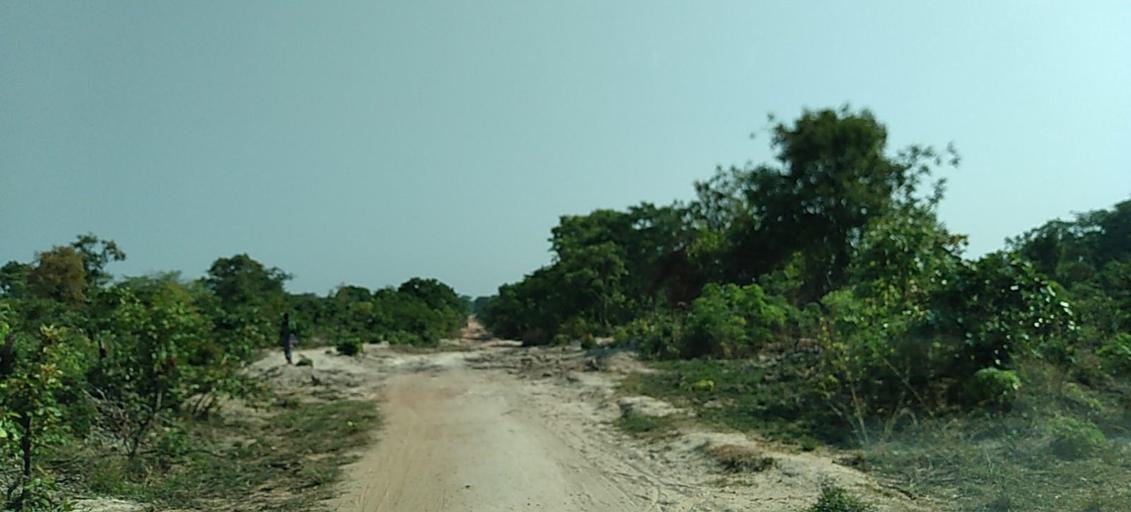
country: ZM
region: Copperbelt
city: Luanshya
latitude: -13.2890
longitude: 28.2522
